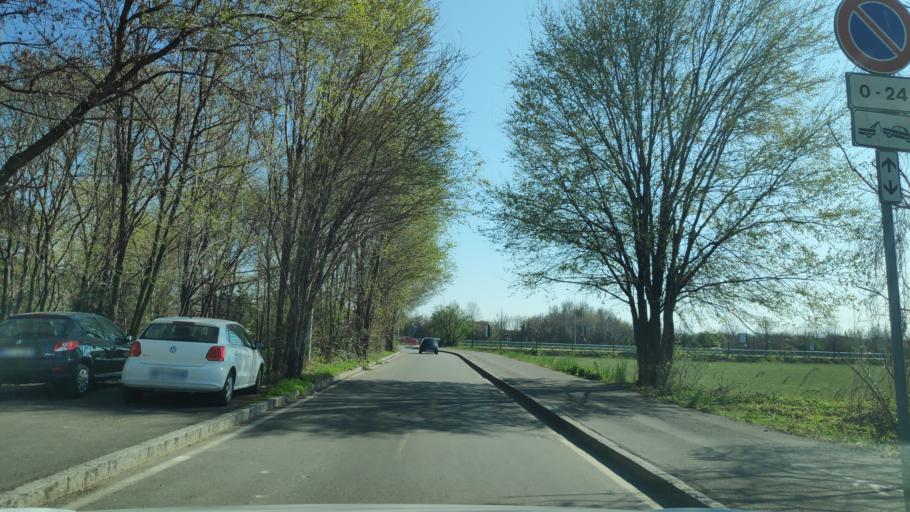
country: IT
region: Lombardy
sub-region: Provincia di Bergamo
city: Orio al Serio
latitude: 45.6868
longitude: 9.6837
